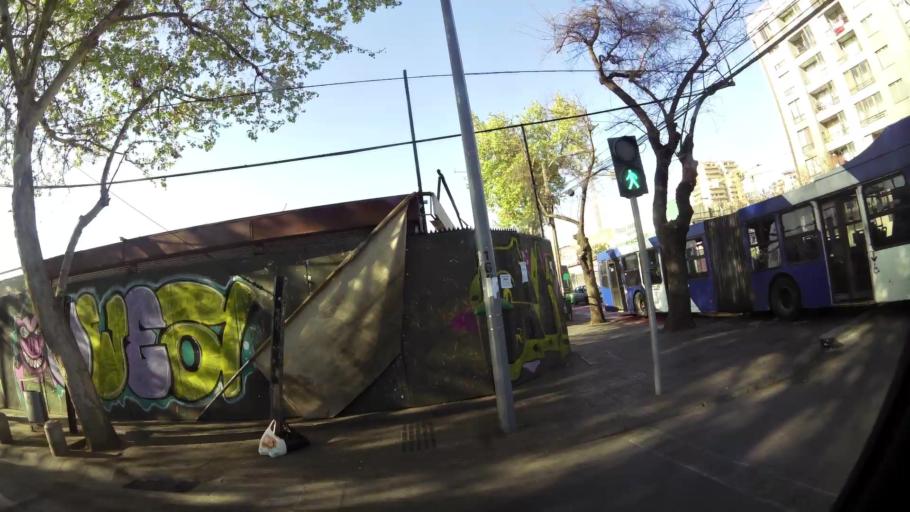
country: CL
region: Santiago Metropolitan
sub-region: Provincia de Santiago
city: Santiago
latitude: -33.4756
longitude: -70.6481
